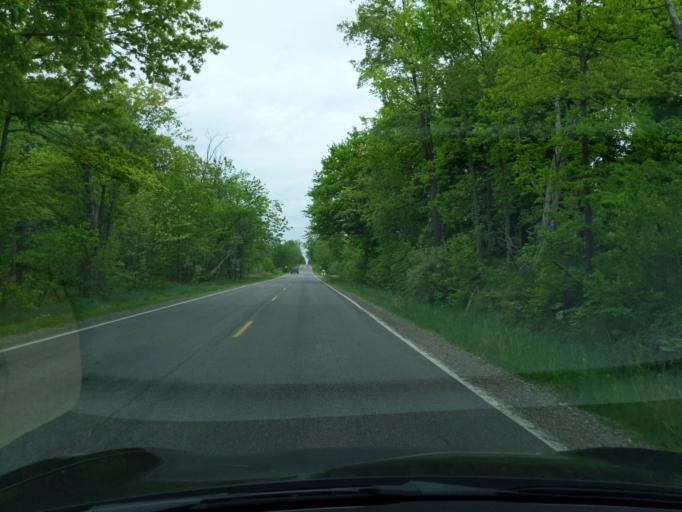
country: US
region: Michigan
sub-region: Ingham County
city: Mason
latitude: 42.5247
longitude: -84.3563
